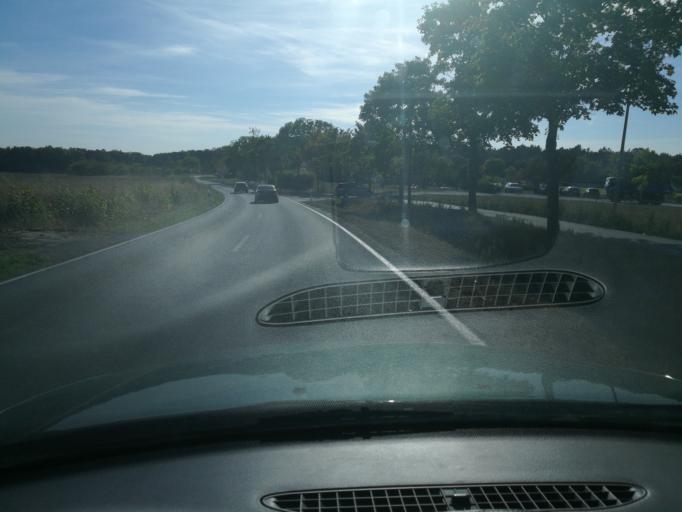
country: DE
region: Bavaria
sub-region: Regierungsbezirk Mittelfranken
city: Kalchreuth
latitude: 49.5537
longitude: 11.1186
